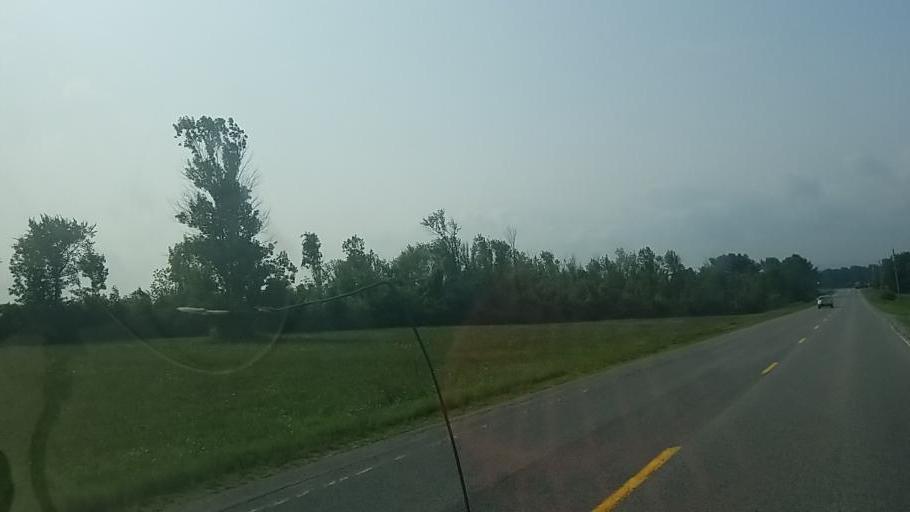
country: US
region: New York
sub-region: Fulton County
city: Johnstown
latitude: 43.0050
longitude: -74.4072
